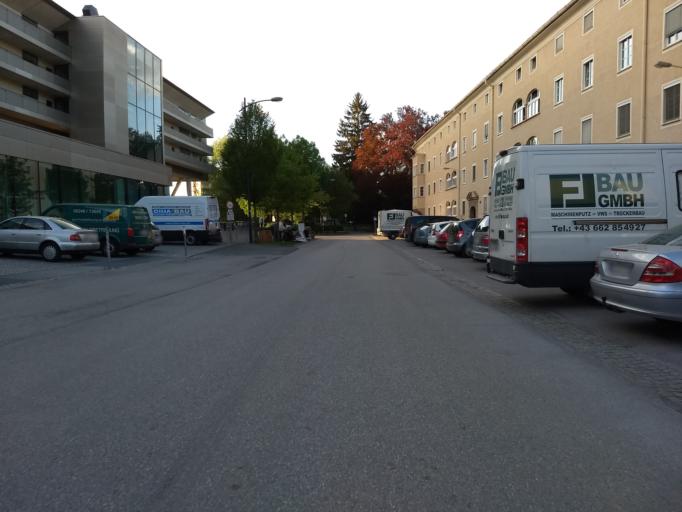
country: AT
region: Salzburg
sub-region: Politischer Bezirk Salzburg-Umgebung
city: Bergheim
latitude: 47.8134
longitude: 13.0285
